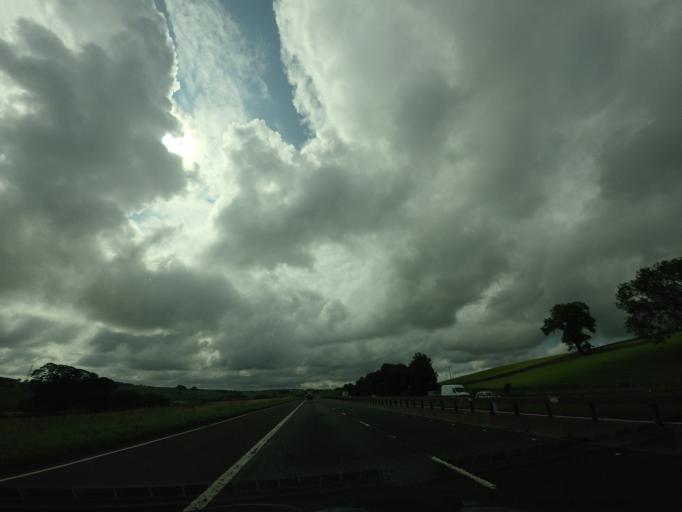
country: GB
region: England
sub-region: Cumbria
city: Penrith
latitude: 54.5718
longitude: -2.6911
